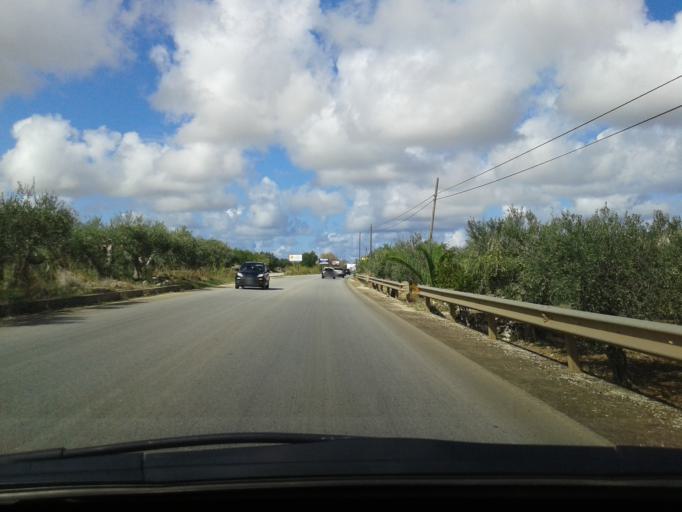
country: IT
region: Sicily
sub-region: Trapani
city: Castelluzzo
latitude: 38.0762
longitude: 12.7318
